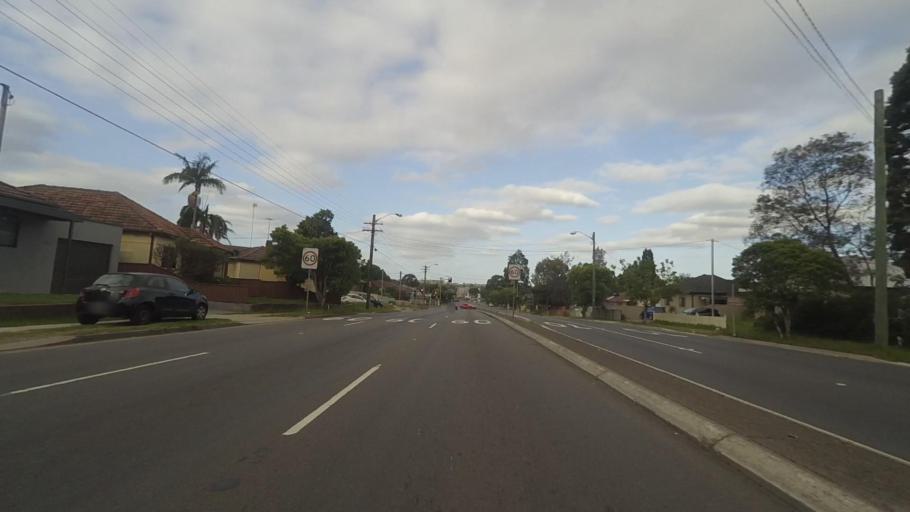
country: AU
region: New South Wales
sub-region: Bankstown
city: Revesby
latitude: -33.9356
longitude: 151.0238
